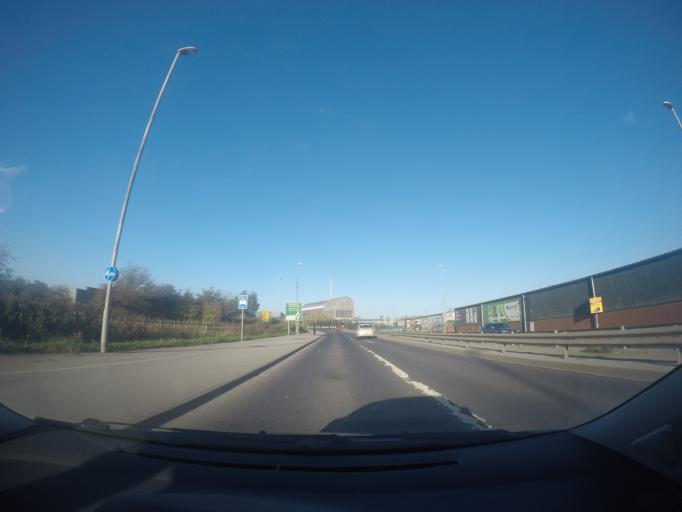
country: GB
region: England
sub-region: City and Borough of Leeds
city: Leeds
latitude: 53.7857
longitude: -1.4975
